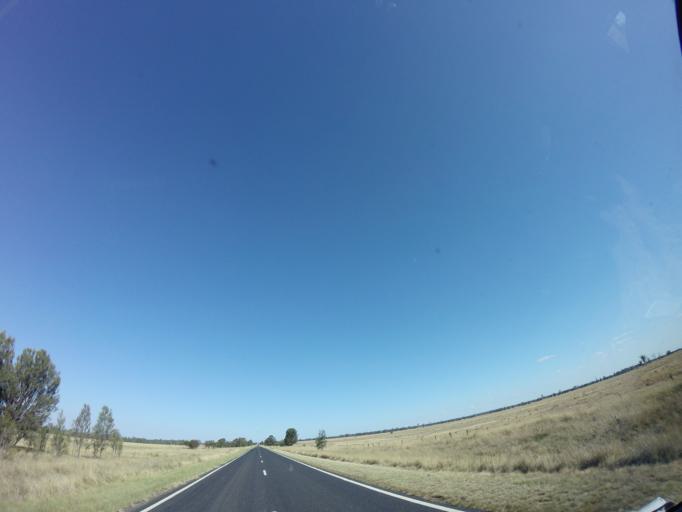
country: AU
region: New South Wales
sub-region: Gilgandra
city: Gilgandra
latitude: -31.6643
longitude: 148.4760
